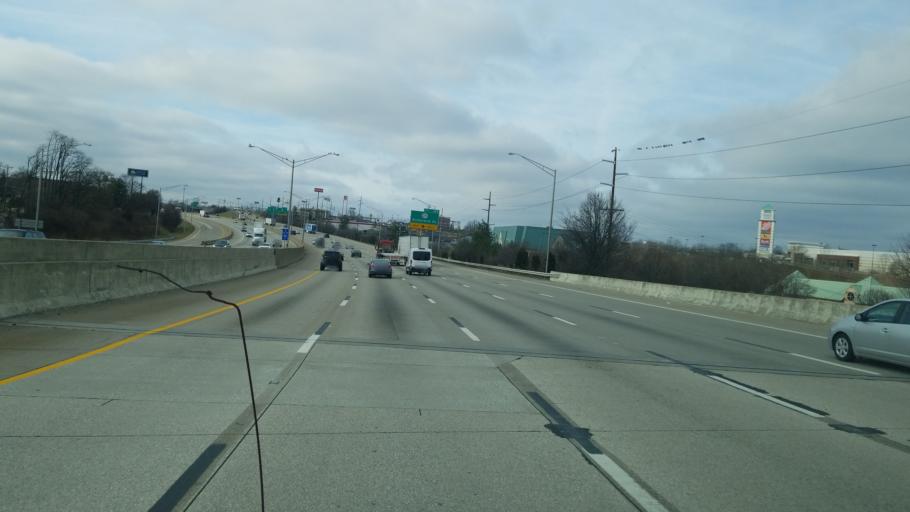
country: US
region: Kentucky
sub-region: Kenton County
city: Crescent Springs
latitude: 39.0513
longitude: -84.5677
